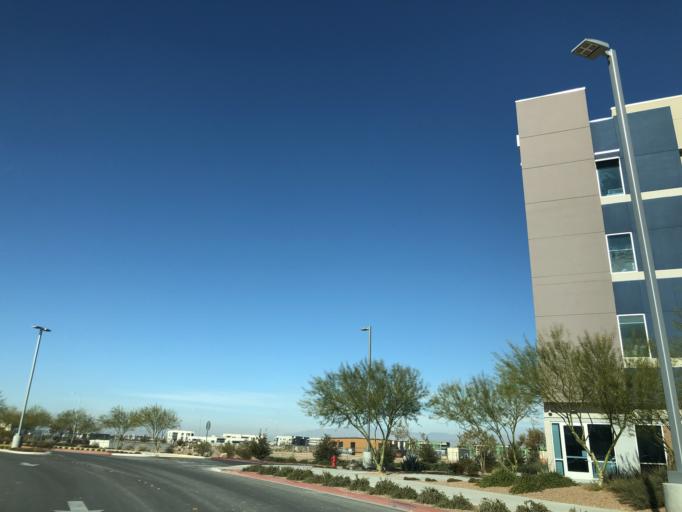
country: US
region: Nevada
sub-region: Clark County
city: Whitney
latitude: 36.0727
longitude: -115.0315
